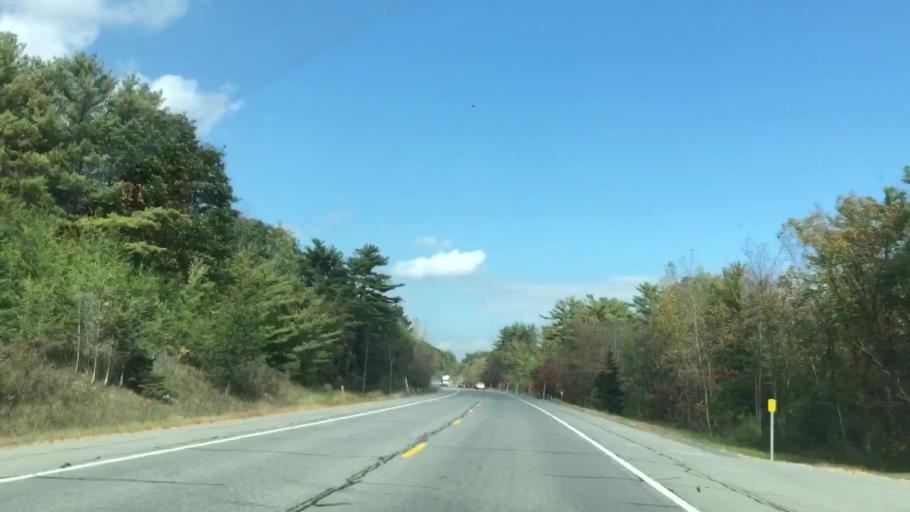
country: US
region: New York
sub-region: Washington County
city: Whitehall
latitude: 43.4463
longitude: -73.4513
